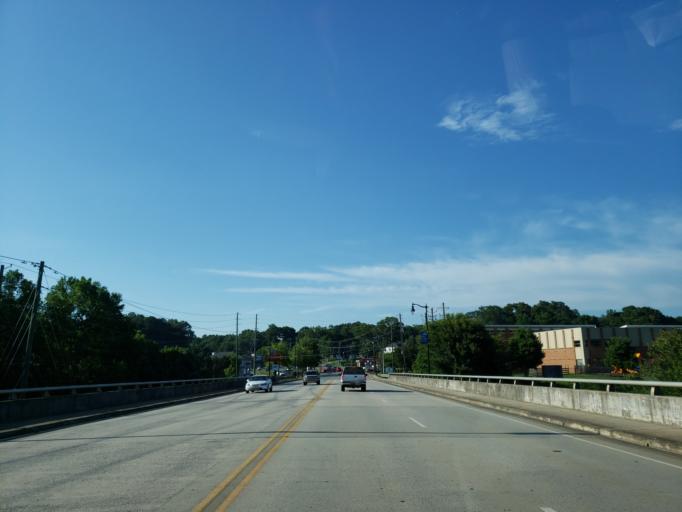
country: US
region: Georgia
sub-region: Cherokee County
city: Canton
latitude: 34.2409
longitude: -84.4943
